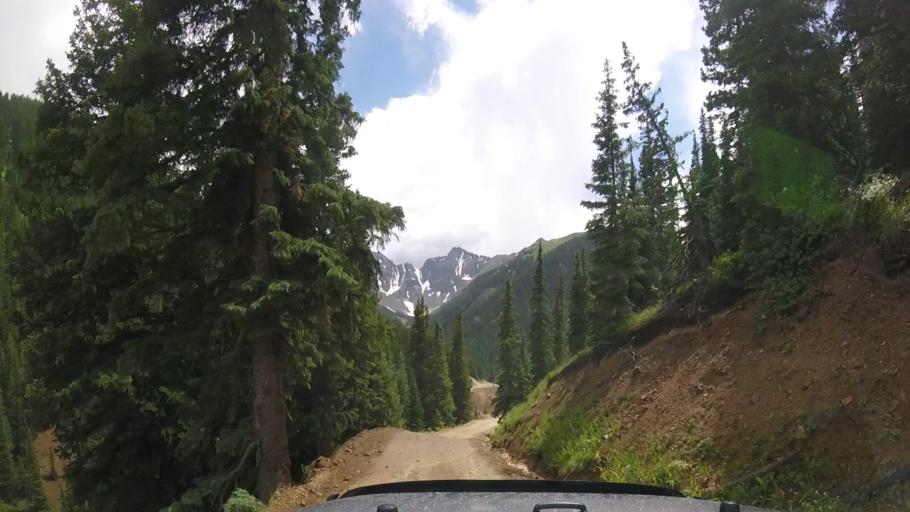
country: US
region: Colorado
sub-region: San Juan County
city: Silverton
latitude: 37.8938
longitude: -107.6485
